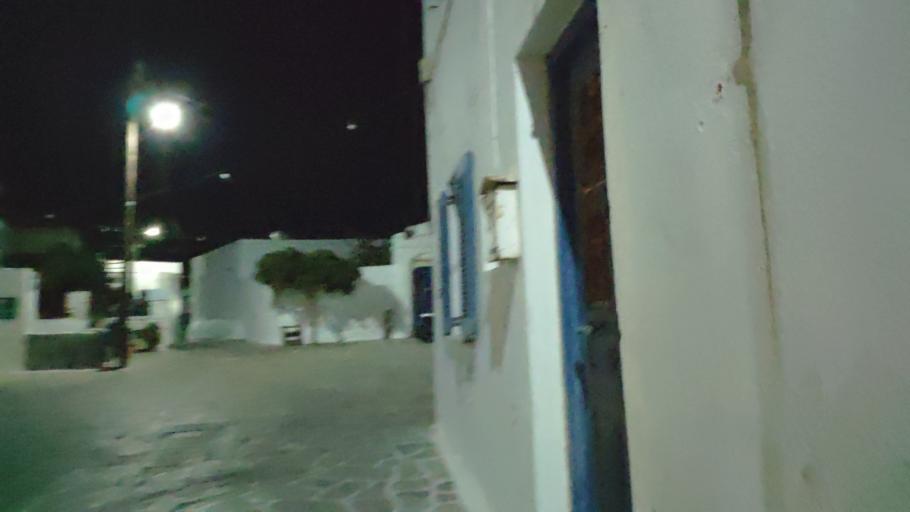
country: GR
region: South Aegean
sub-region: Nomos Kykladon
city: Kythnos
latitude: 37.4125
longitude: 24.4323
